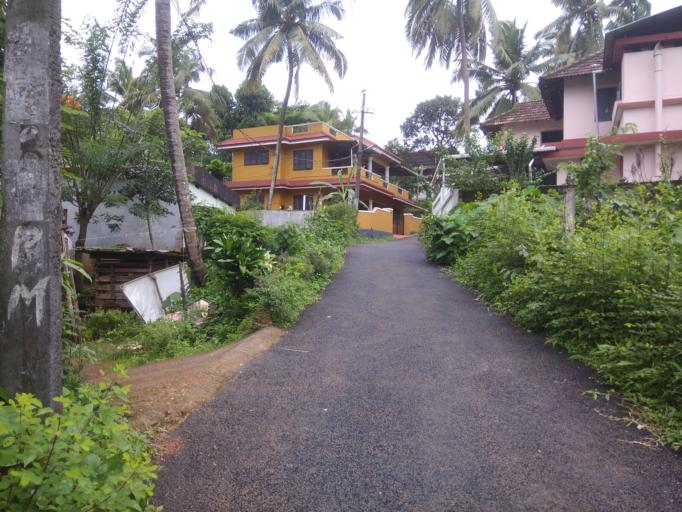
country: IN
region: Kerala
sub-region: Thrissur District
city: Avanoor
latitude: 10.5589
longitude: 76.1723
